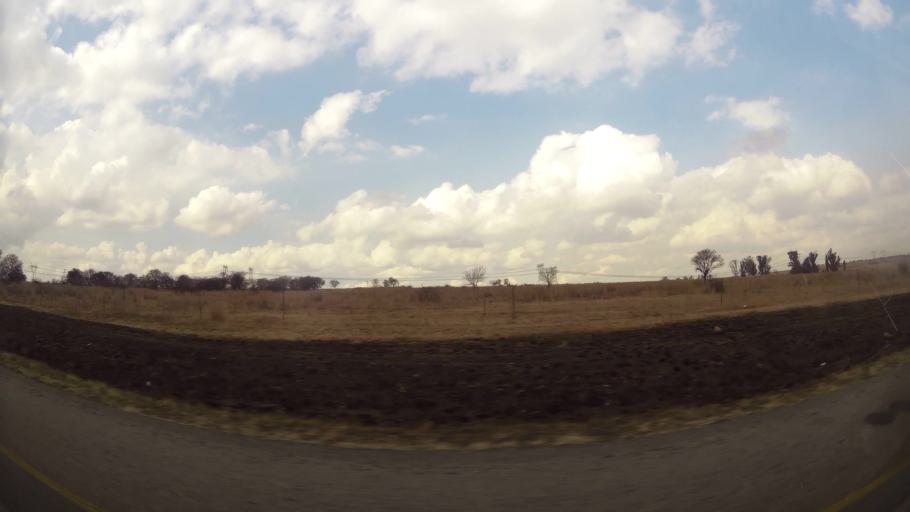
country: ZA
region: Orange Free State
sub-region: Fezile Dabi District Municipality
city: Sasolburg
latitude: -26.7962
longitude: 27.9157
